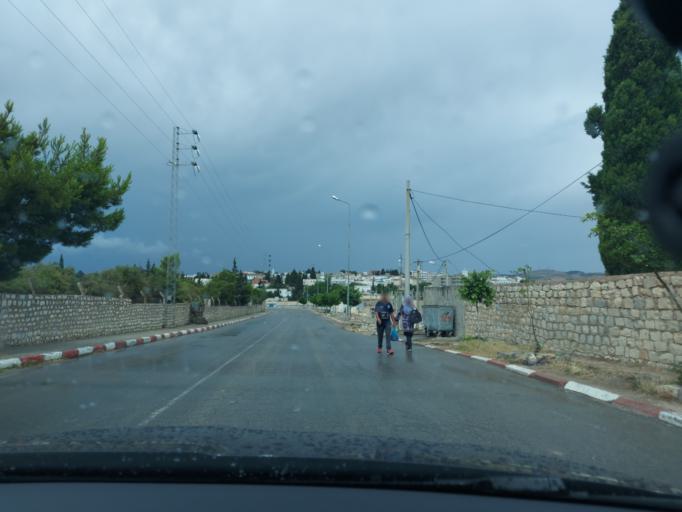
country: TN
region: Silyanah
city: Maktar
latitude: 35.8566
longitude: 9.2086
